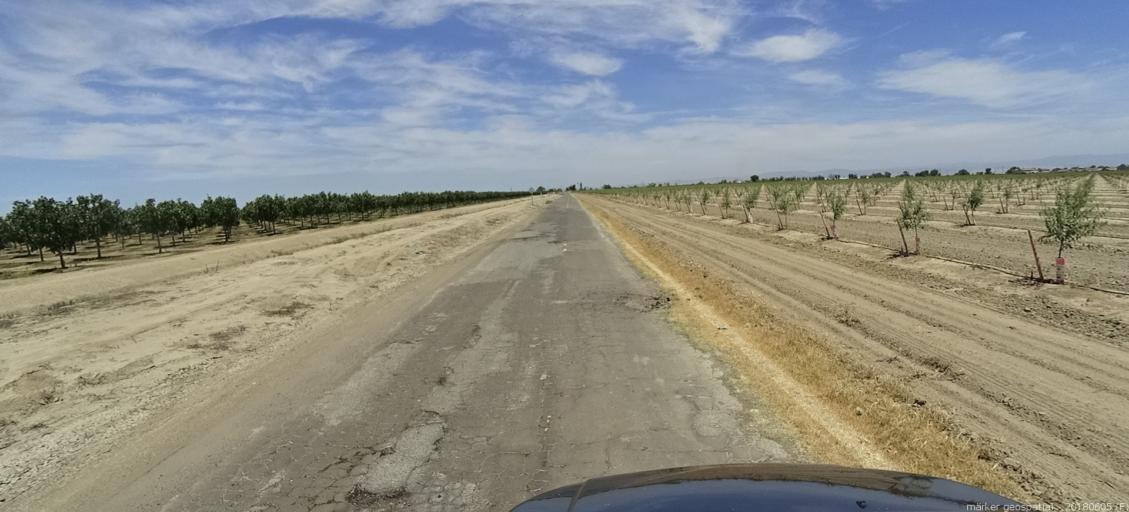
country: US
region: California
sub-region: Madera County
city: Chowchilla
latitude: 37.1136
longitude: -120.2928
